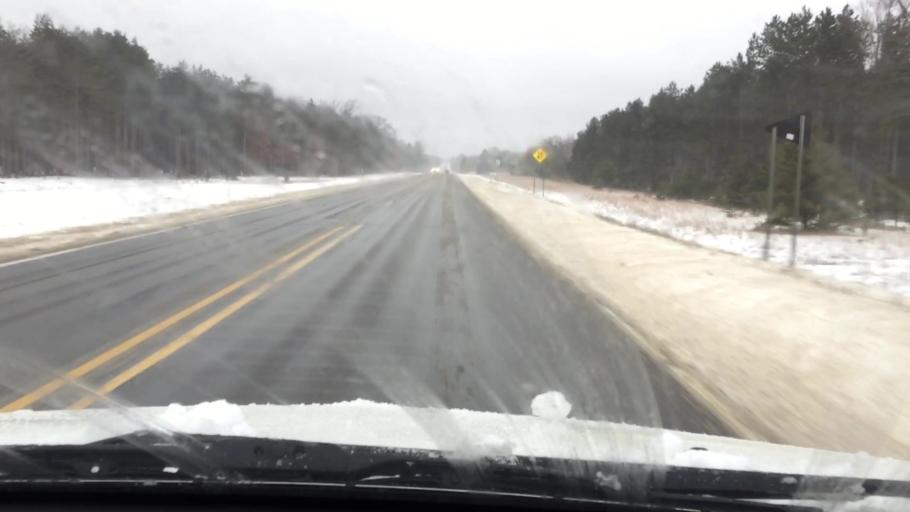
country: US
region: Michigan
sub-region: Wexford County
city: Manton
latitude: 44.4762
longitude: -85.4066
